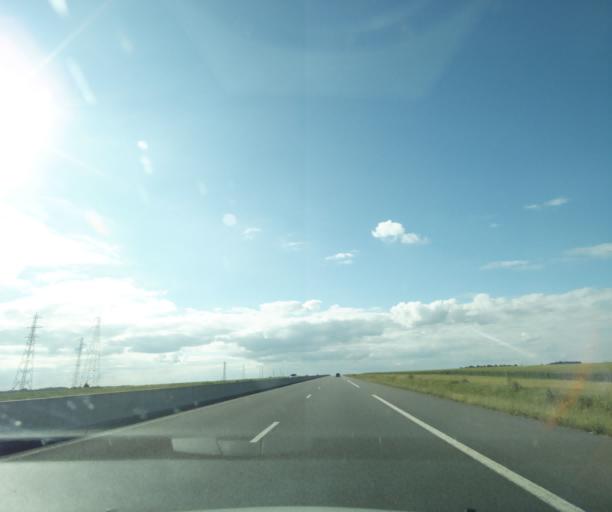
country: FR
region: Centre
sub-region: Departement d'Eure-et-Loir
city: Voves
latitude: 48.3385
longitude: 1.6384
